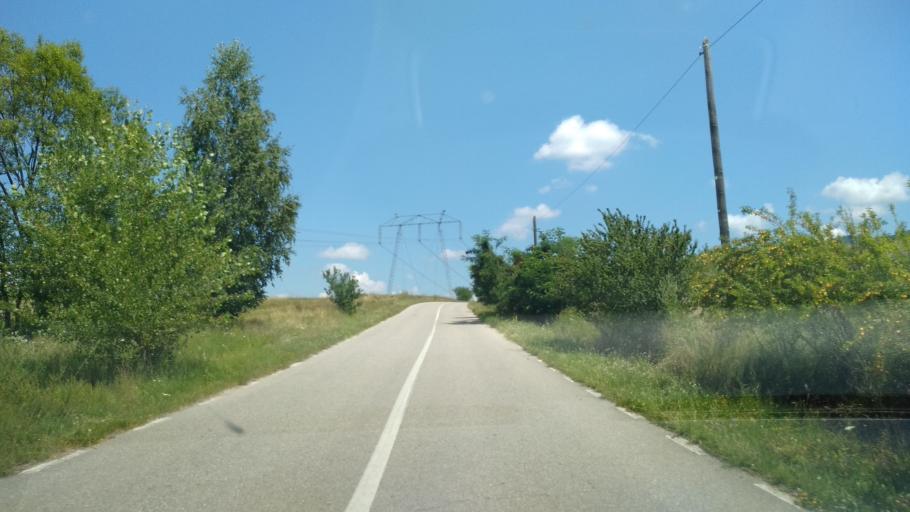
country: RO
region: Hunedoara
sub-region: Comuna Santamaria-Orlea
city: Santamaria-Orlea
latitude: 45.5890
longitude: 22.9946
